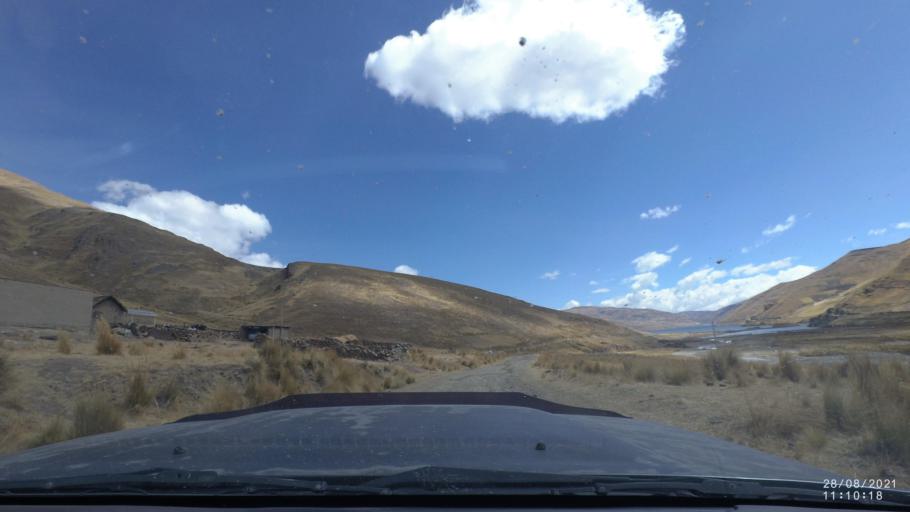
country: BO
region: Cochabamba
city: Cochabamba
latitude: -17.1573
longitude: -66.3106
